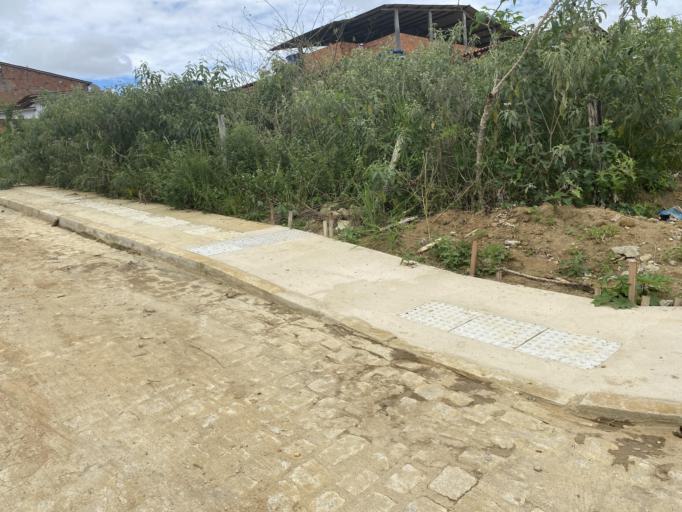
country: BR
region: Bahia
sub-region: Mutuipe
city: Mutuipe
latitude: -13.2555
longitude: -39.5660
